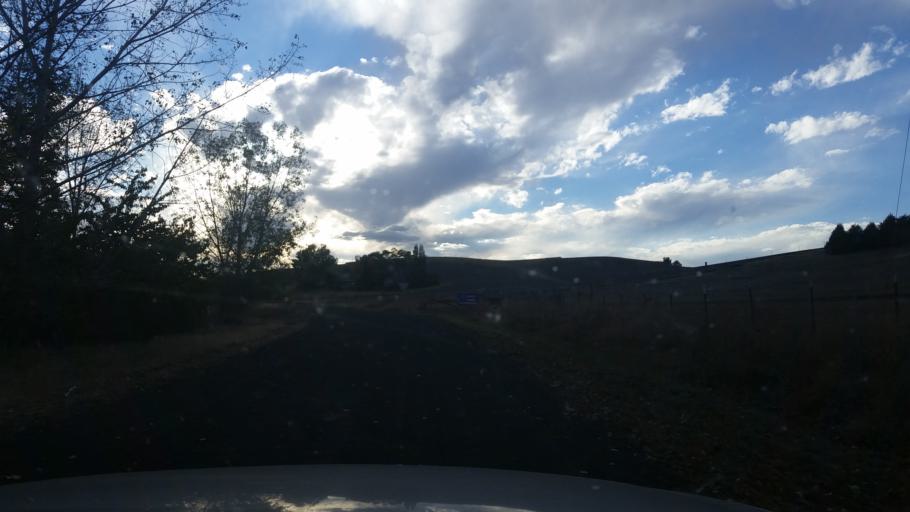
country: US
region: Washington
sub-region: Spokane County
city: Cheney
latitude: 47.4724
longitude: -117.6167
